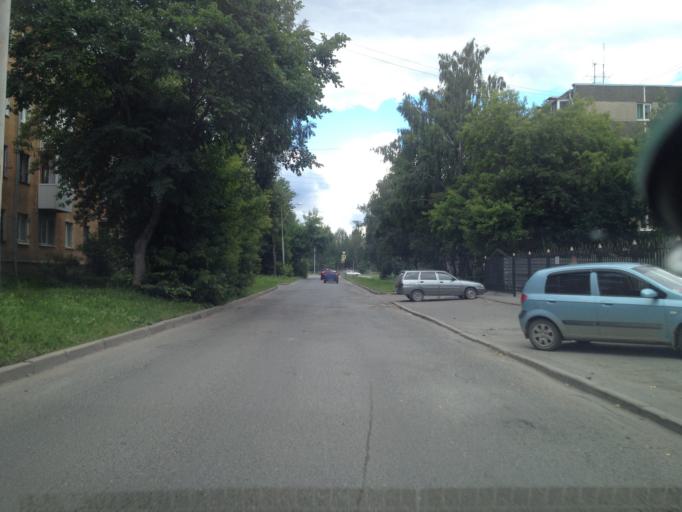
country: RU
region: Sverdlovsk
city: Shuvakish
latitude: 56.8714
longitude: 60.5301
